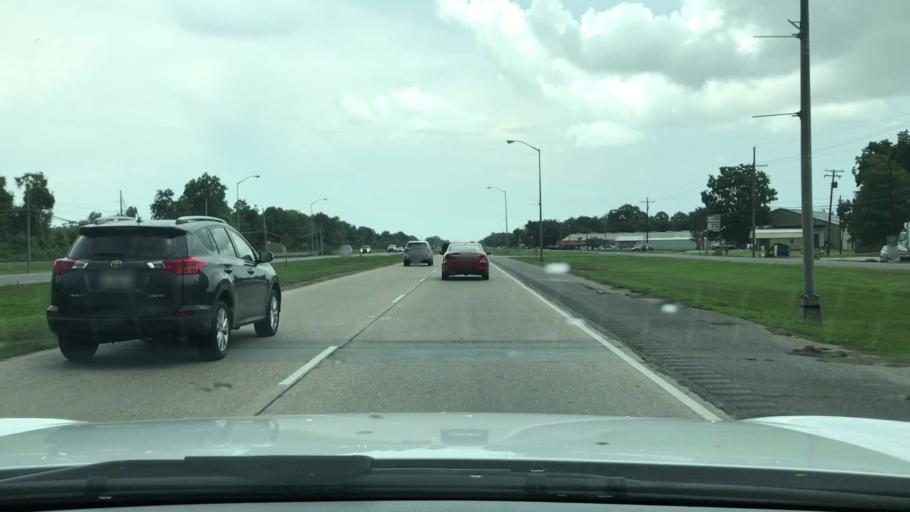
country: US
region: Louisiana
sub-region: Iberville Parish
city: Plaquemine
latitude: 30.3050
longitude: -91.2447
